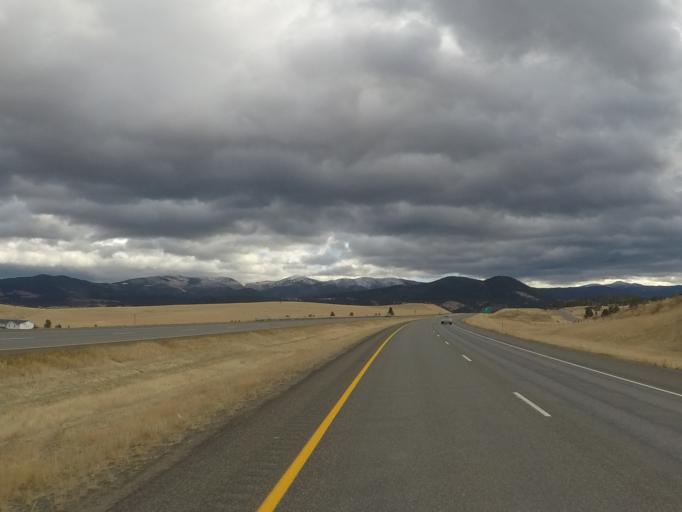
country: US
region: Montana
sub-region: Jefferson County
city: Montana City
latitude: 46.5593
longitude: -111.9538
